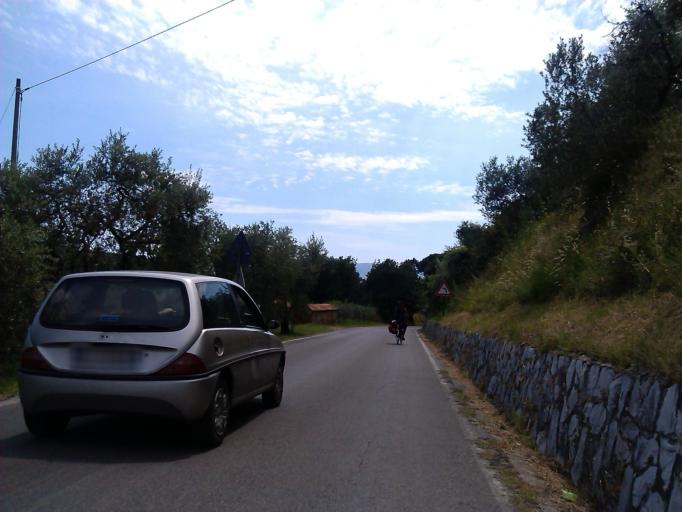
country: IT
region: Tuscany
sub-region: Provincia di Prato
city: Montemurlo
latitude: 43.9610
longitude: 11.0439
